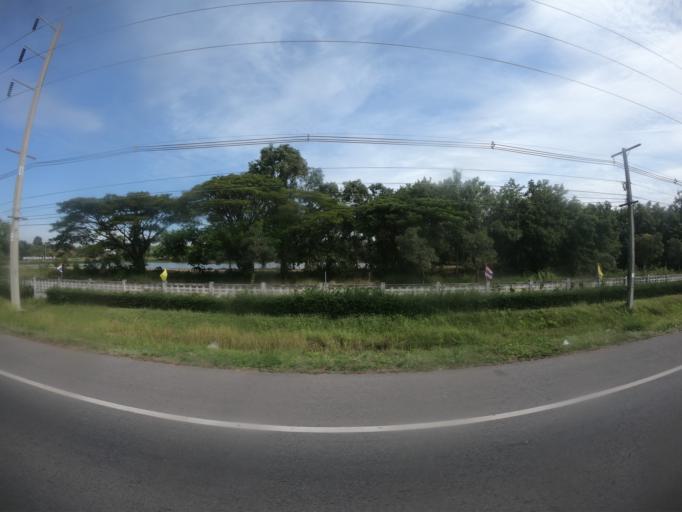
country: TH
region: Maha Sarakham
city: Chiang Yuen
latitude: 16.4394
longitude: 103.0470
